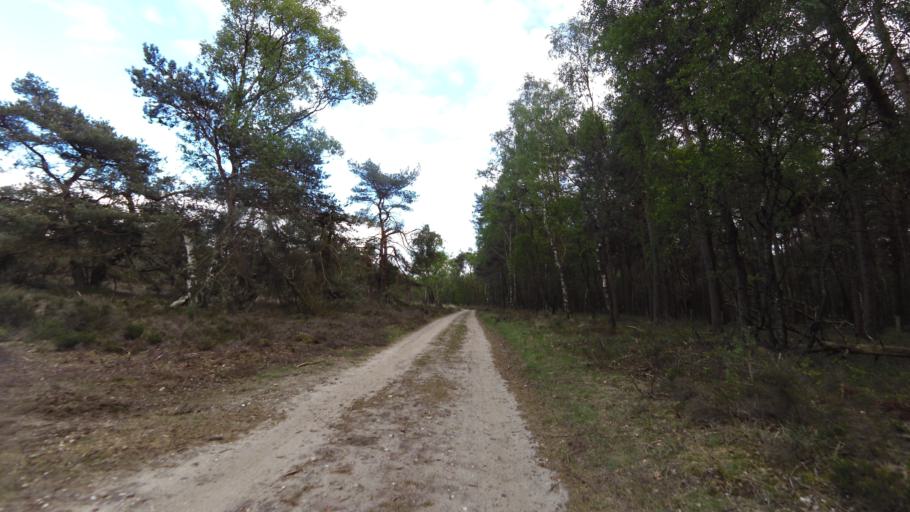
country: NL
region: Gelderland
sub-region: Gemeente Rozendaal
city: Rozendaal
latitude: 52.0410
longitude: 5.9575
